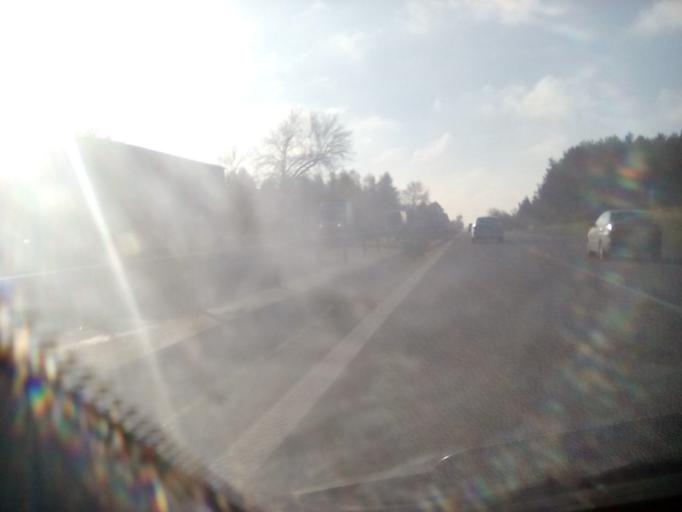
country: PL
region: Masovian Voivodeship
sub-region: Powiat piaseczynski
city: Tarczyn
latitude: 51.9238
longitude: 20.8516
